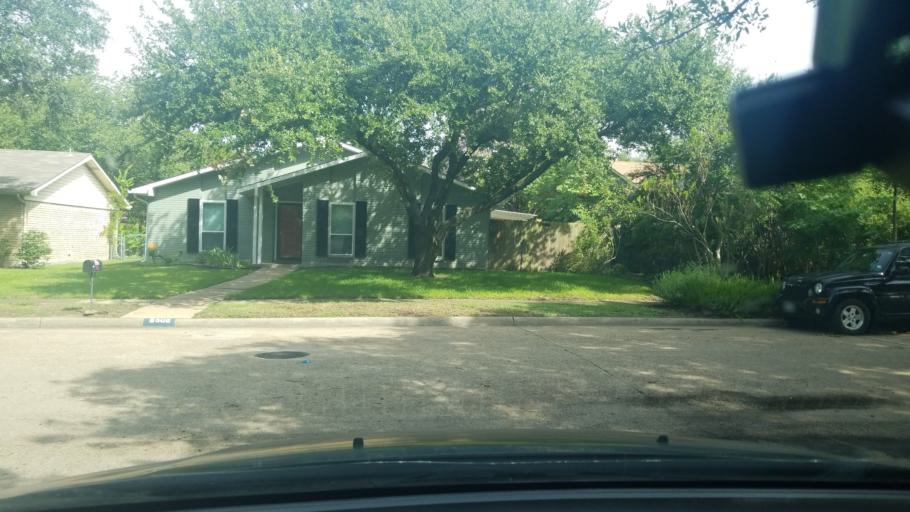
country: US
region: Texas
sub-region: Dallas County
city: Highland Park
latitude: 32.8050
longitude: -96.6947
